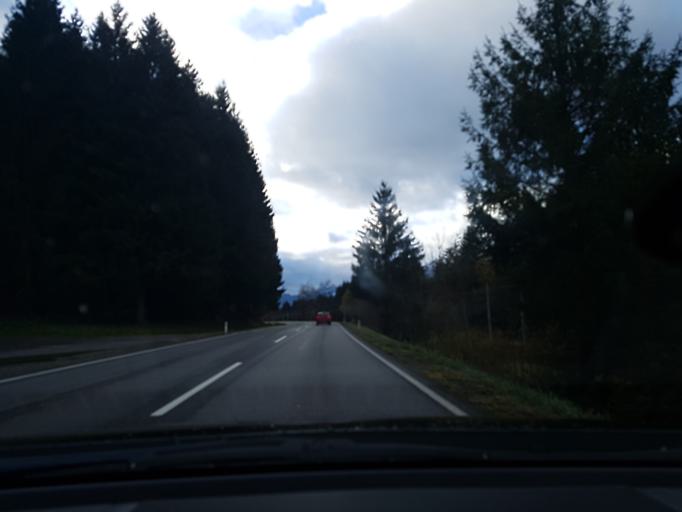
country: AT
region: Styria
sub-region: Politischer Bezirk Liezen
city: Lassing
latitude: 47.5495
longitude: 14.2902
